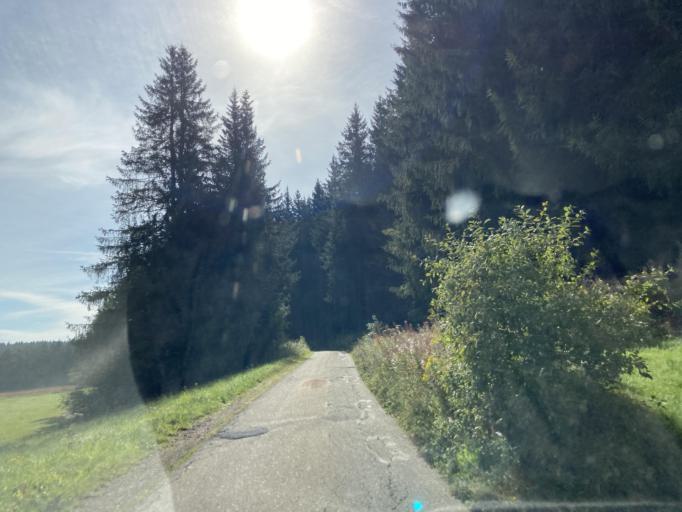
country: DE
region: Baden-Wuerttemberg
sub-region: Freiburg Region
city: Schonwald im Schwarzwald
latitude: 48.0916
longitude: 8.2304
